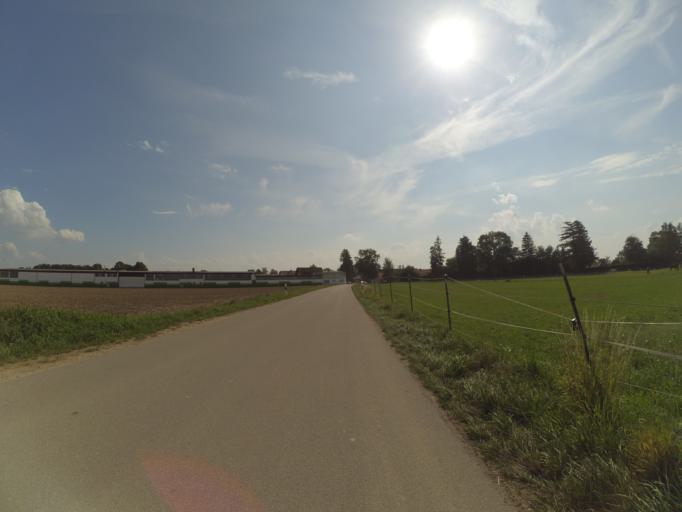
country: DE
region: Bavaria
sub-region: Swabia
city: Lamerdingen
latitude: 48.0887
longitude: 10.7701
